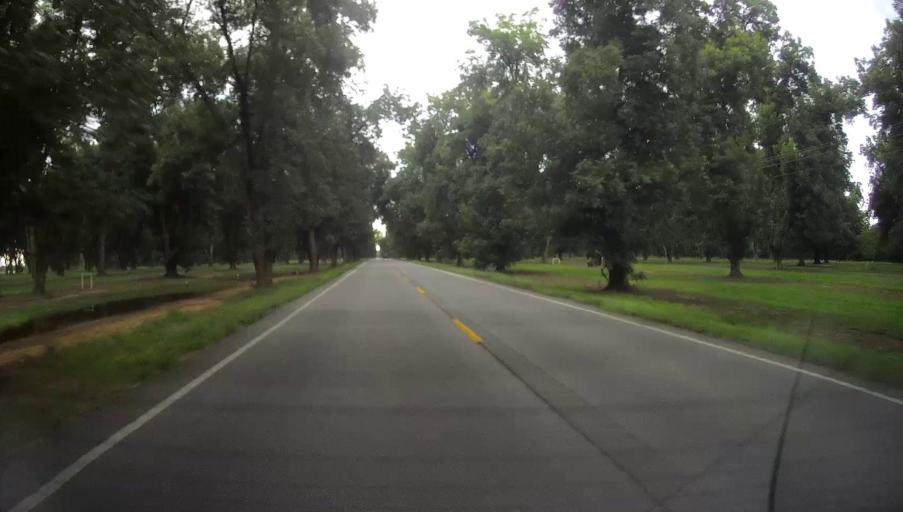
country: US
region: Georgia
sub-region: Houston County
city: Perry
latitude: 32.4405
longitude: -83.6573
